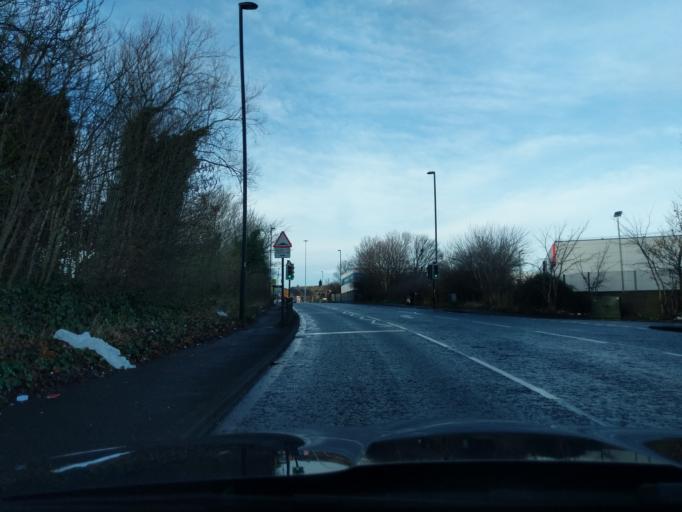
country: GB
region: England
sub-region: Gateshead
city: Felling
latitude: 54.9762
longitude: -1.5713
